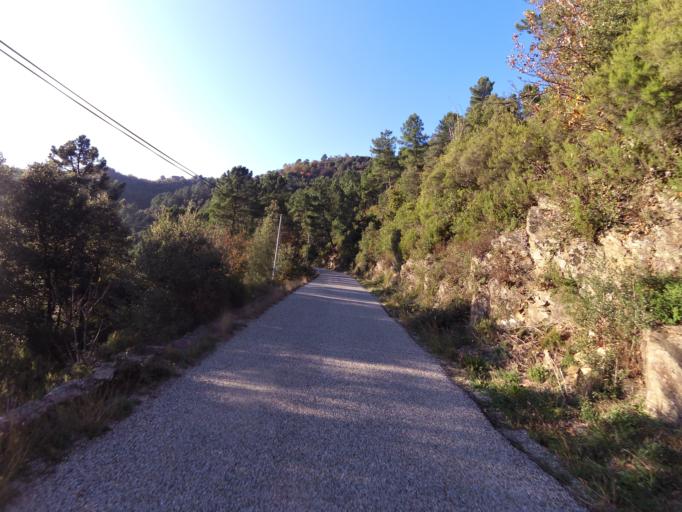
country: FR
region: Rhone-Alpes
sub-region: Departement de l'Ardeche
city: Lablachere
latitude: 44.5242
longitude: 4.1697
